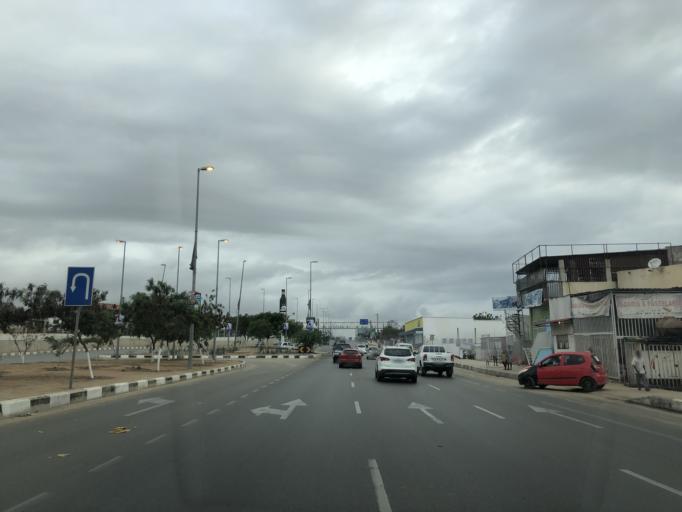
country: AO
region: Luanda
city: Luanda
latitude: -8.8673
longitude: 13.2130
